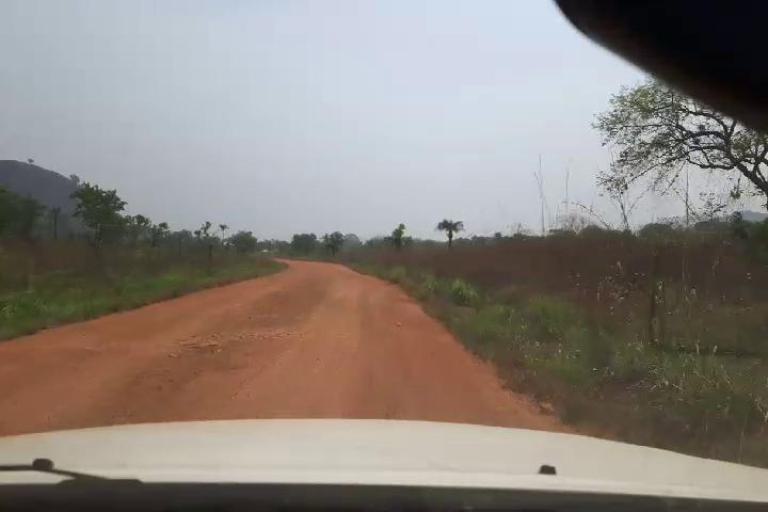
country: SL
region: Northern Province
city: Bumbuna
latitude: 8.9543
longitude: -11.8054
